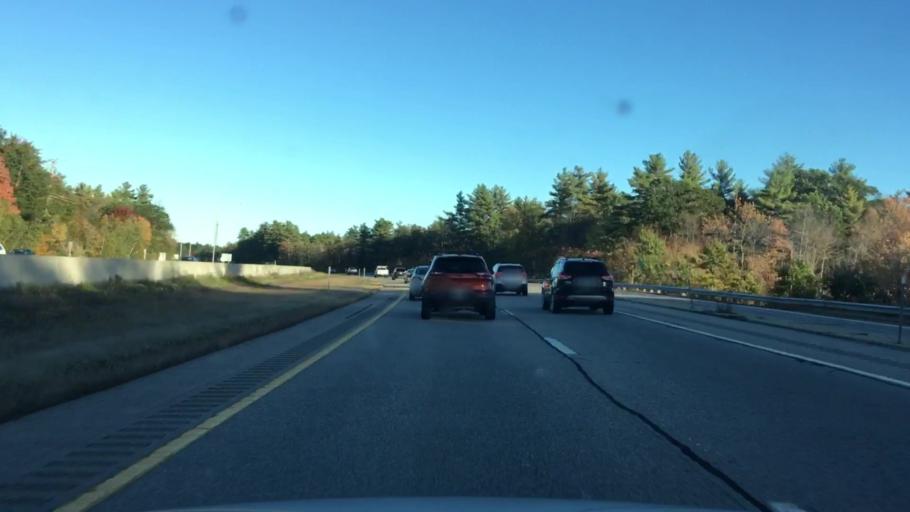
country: US
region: New Hampshire
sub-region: Rockingham County
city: Epping
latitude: 43.0257
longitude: -71.1132
